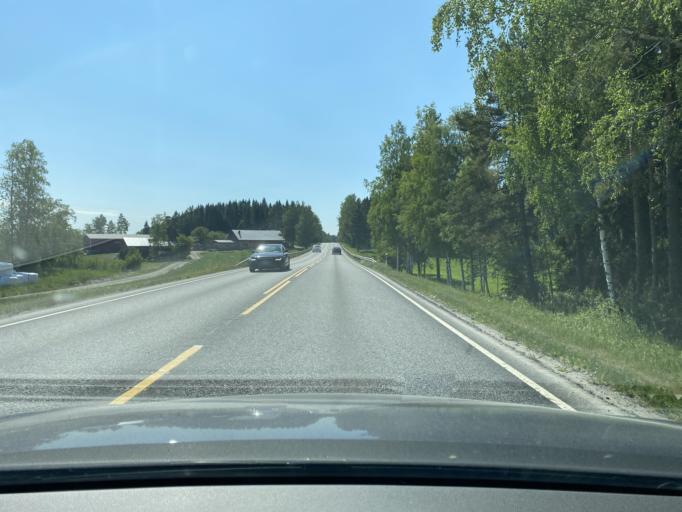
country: FI
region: Pirkanmaa
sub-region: Tampere
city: Nokia
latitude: 61.4144
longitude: 23.3131
